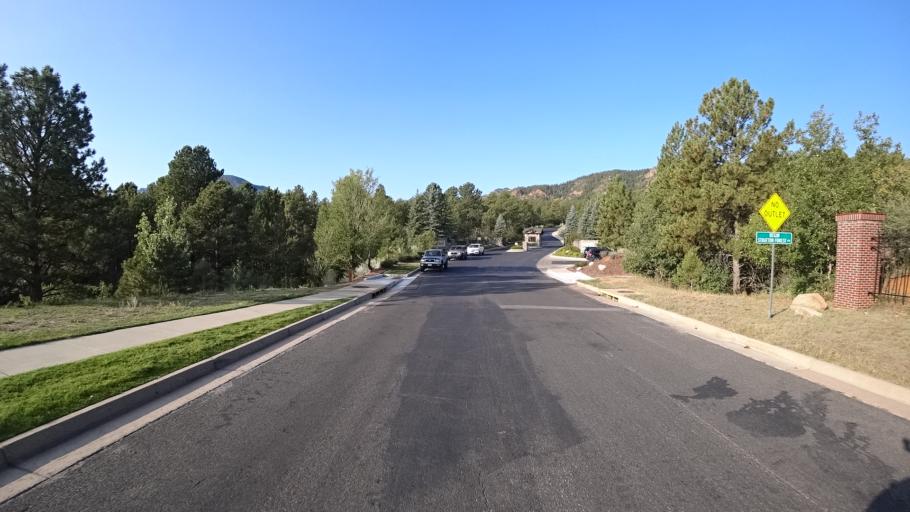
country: US
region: Colorado
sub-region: El Paso County
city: Colorado Springs
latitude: 38.8046
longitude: -104.8621
